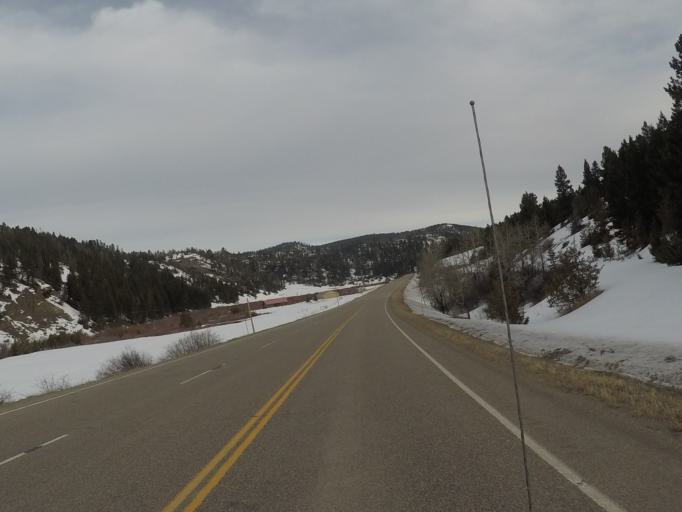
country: US
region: Montana
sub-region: Meagher County
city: White Sulphur Springs
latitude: 46.6693
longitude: -110.8775
